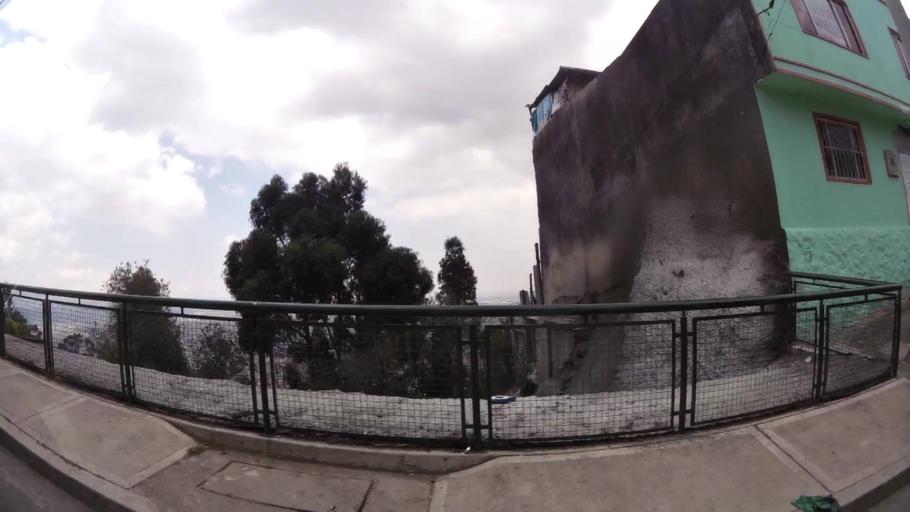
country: CO
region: Bogota D.C.
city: Bogota
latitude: 4.5811
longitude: -74.0730
